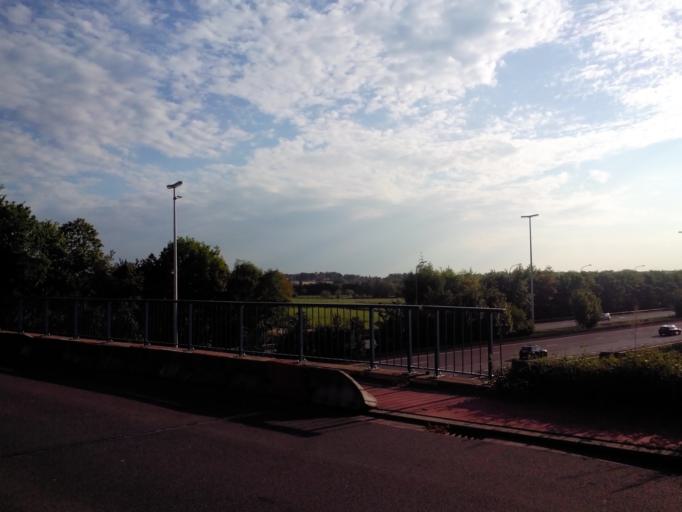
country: BE
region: Flanders
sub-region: Provincie Vlaams-Brabant
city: Bierbeek
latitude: 50.8446
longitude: 4.7282
